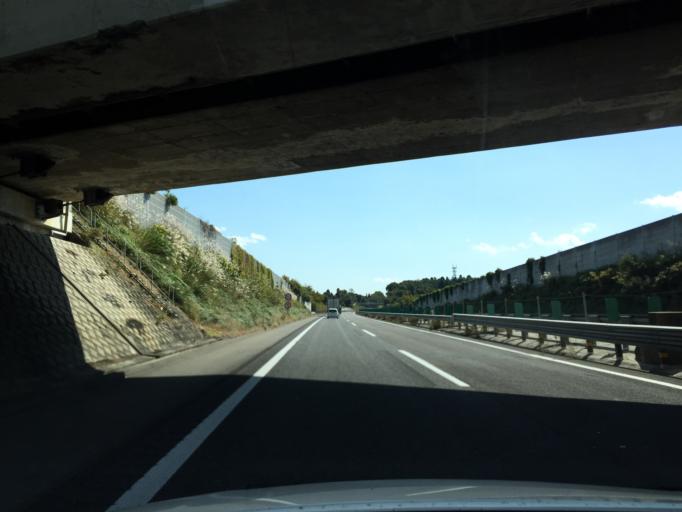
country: JP
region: Fukushima
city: Koriyama
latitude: 37.3442
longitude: 140.3325
